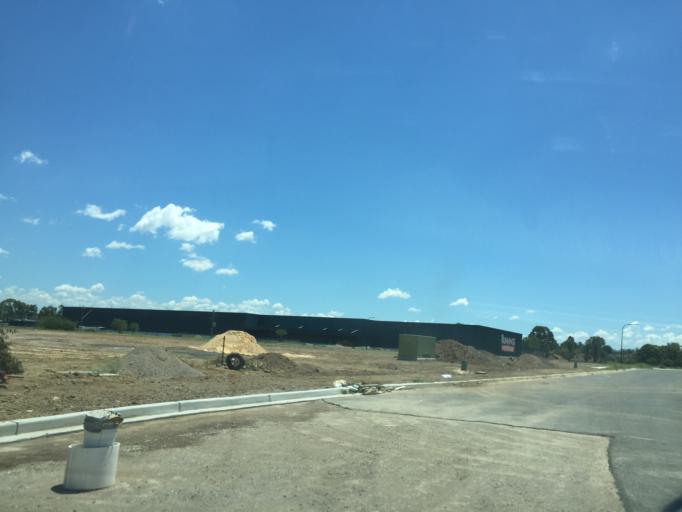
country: AU
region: New South Wales
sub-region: Blacktown
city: Mount Druitt
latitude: -33.7816
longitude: 150.8117
